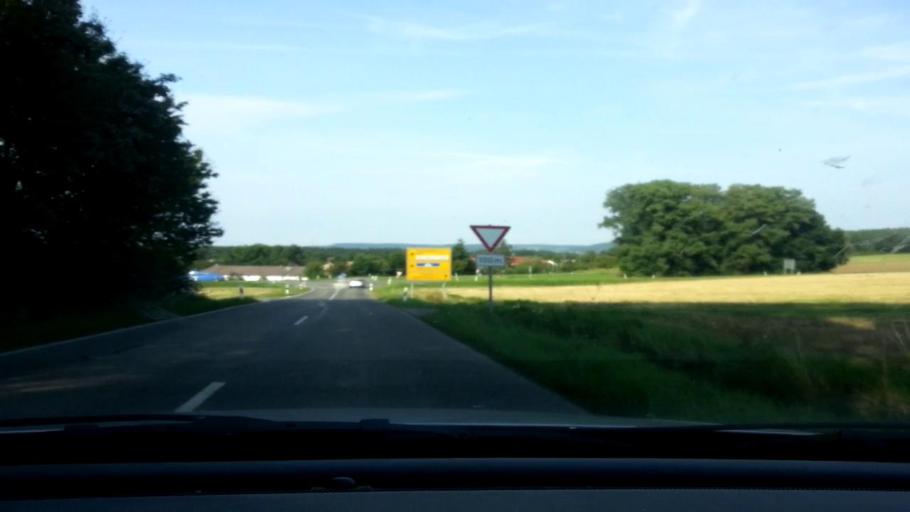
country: DE
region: Bavaria
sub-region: Upper Franconia
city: Zapfendorf
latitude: 49.9974
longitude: 10.9652
